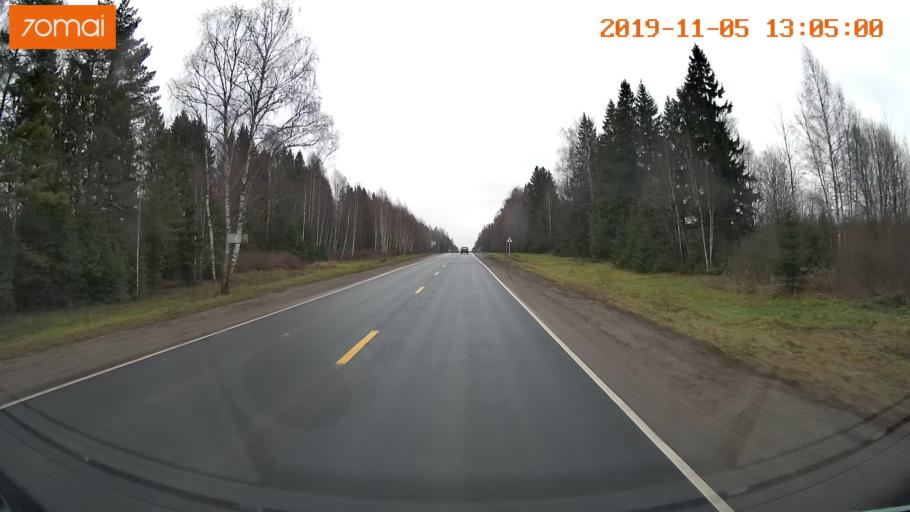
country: RU
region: Ivanovo
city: Kitovo
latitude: 56.8854
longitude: 41.2332
